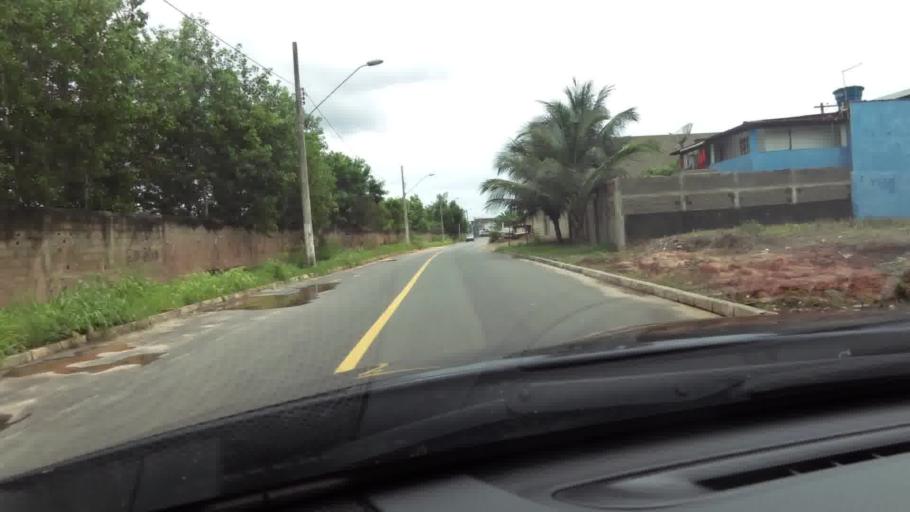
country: BR
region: Espirito Santo
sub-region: Guarapari
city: Guarapari
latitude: -20.6563
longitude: -40.5007
